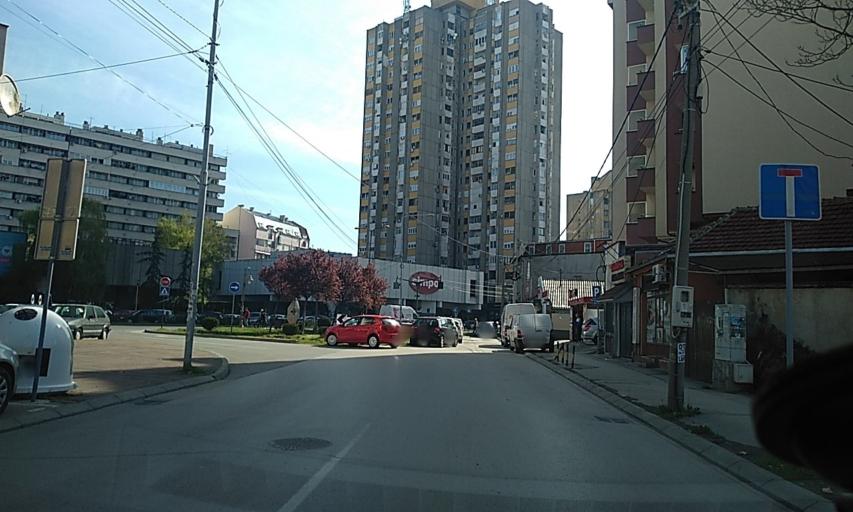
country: RS
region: Central Serbia
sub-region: Nisavski Okrug
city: Nis
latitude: 43.3186
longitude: 21.9078
